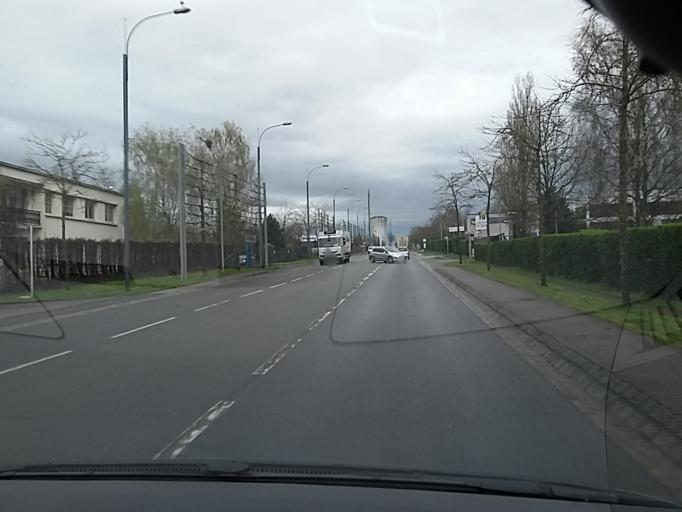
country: FR
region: Picardie
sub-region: Departement de la Somme
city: Amiens
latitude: 49.9324
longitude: 2.2753
